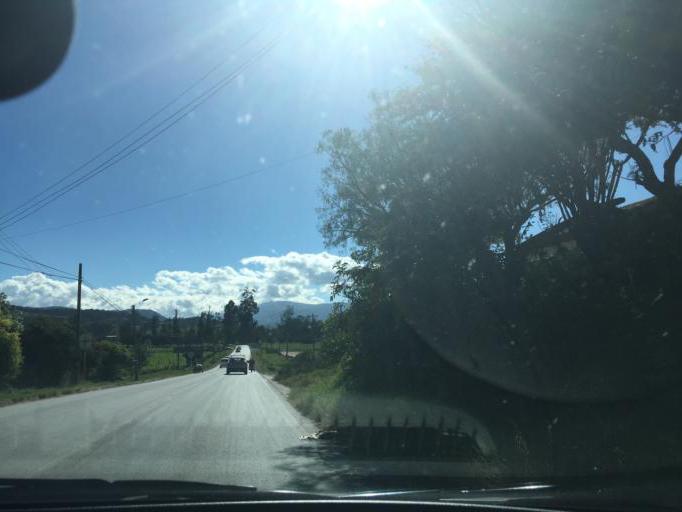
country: CO
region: Boyaca
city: Firavitoba
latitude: 5.6743
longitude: -72.9605
